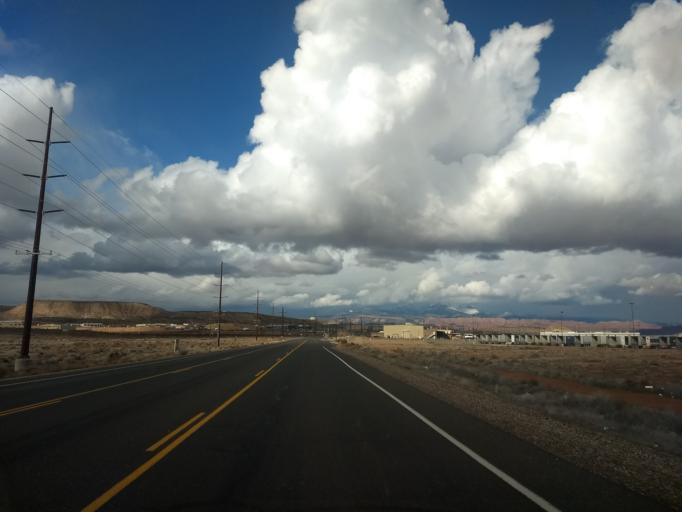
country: US
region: Utah
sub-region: Washington County
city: Saint George
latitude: 37.0237
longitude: -113.5630
